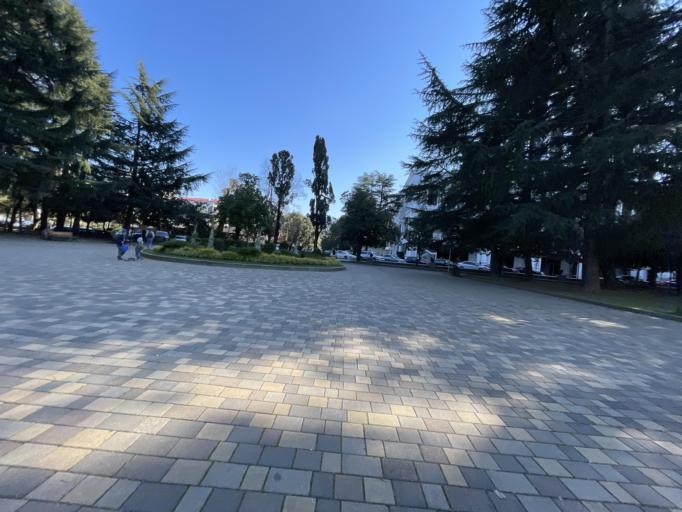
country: GE
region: Ajaria
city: Batumi
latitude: 41.6519
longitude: 41.6305
